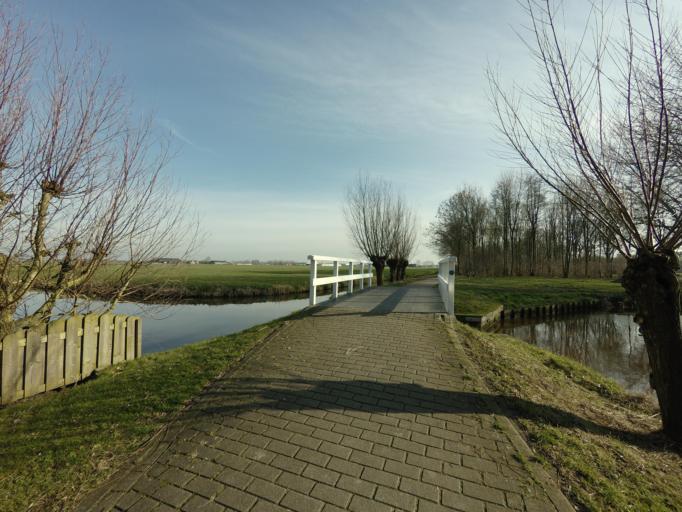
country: NL
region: South Holland
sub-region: Gemeente Giessenlanden
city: Giessenburg
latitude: 51.8509
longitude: 4.8957
